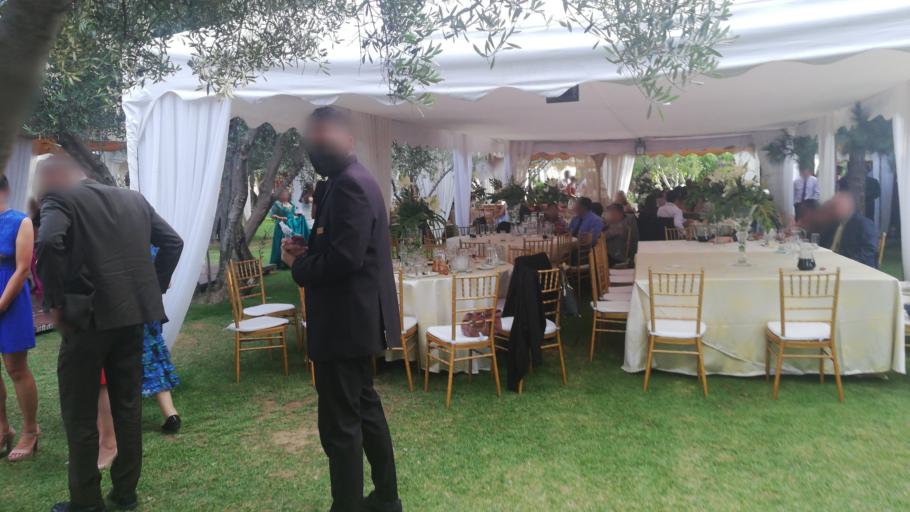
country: BO
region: Cochabamba
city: Cochabamba
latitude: -17.3353
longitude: -66.2405
